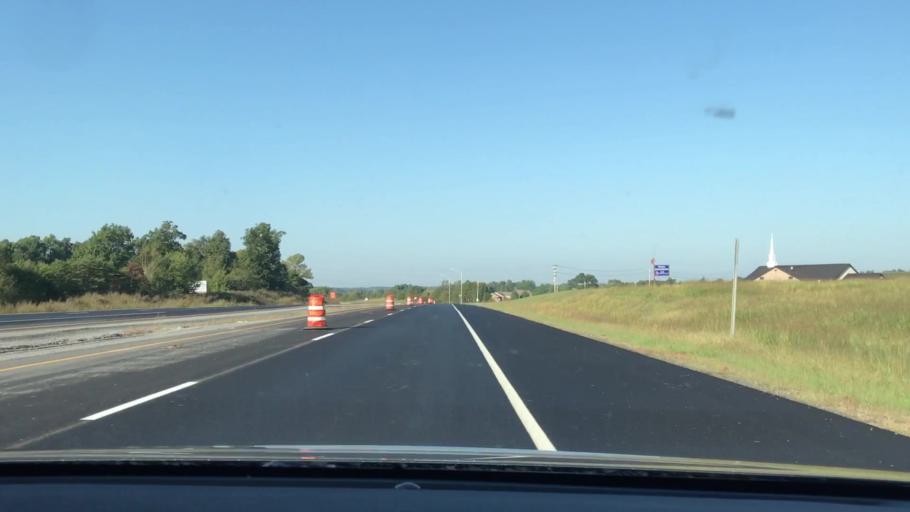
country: US
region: Kentucky
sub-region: Trigg County
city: Cadiz
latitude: 36.8606
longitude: -87.8052
